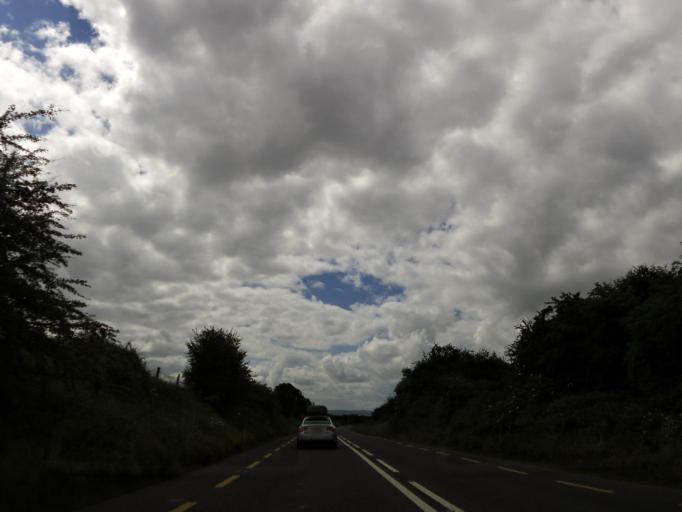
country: IE
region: Munster
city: Nenagh Bridge
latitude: 52.9181
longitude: -8.1747
